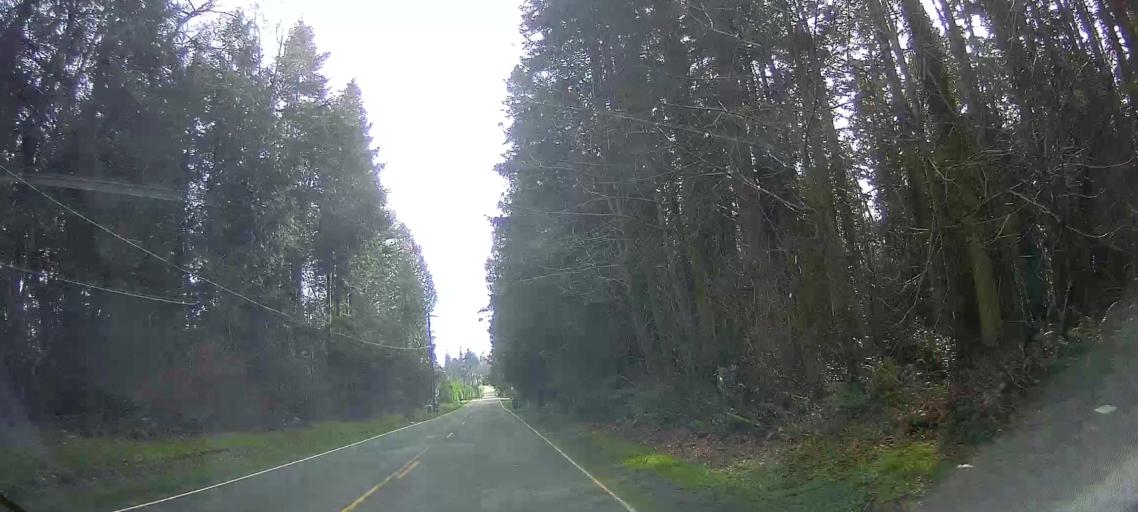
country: US
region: Washington
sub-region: Island County
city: Langley
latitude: 48.0993
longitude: -122.4154
